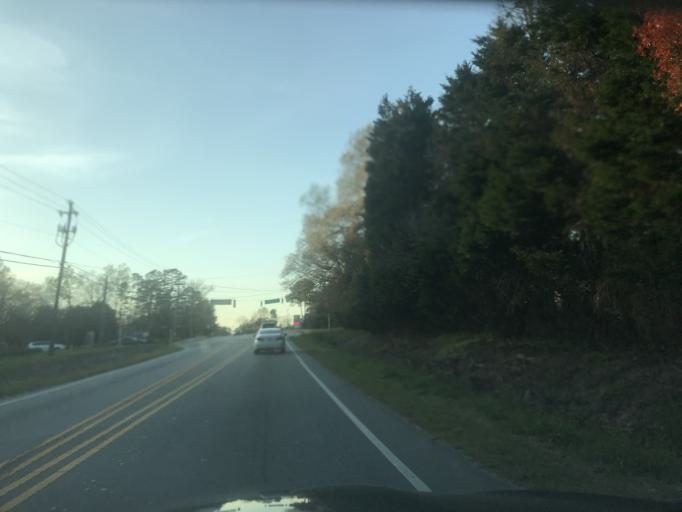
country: US
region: North Carolina
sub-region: Wake County
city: Knightdale
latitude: 35.7599
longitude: -78.5511
